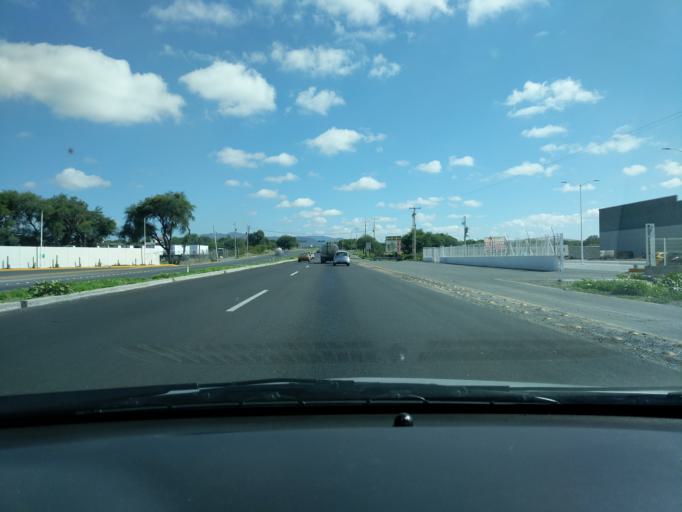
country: MX
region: Queretaro
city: Tlacote el Bajo
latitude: 20.6445
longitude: -100.5011
